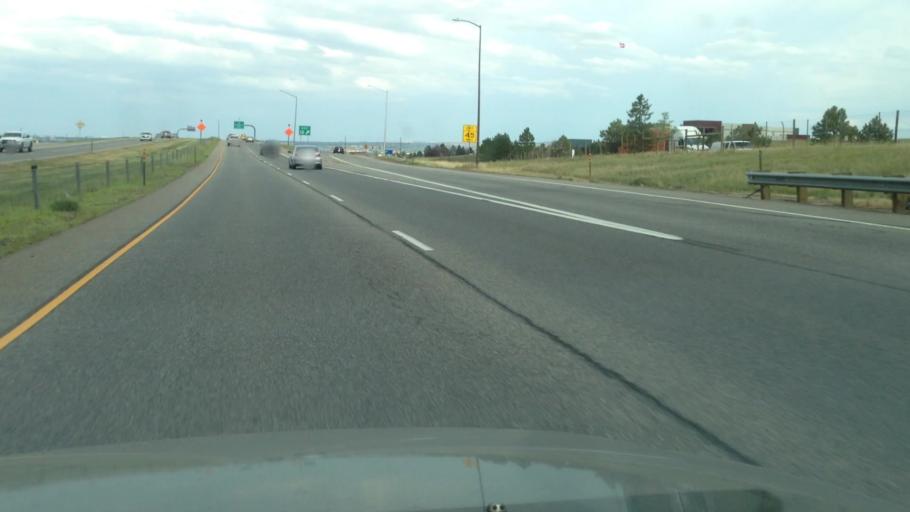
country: US
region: Colorado
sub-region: Jefferson County
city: Ken Caryl
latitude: 39.5602
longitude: -105.1157
